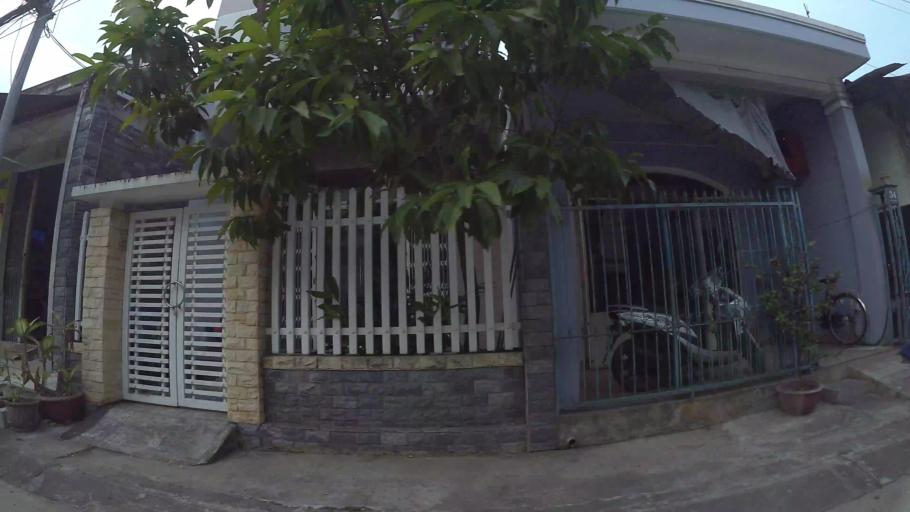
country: VN
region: Da Nang
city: Cam Le
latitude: 16.0208
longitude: 108.2033
